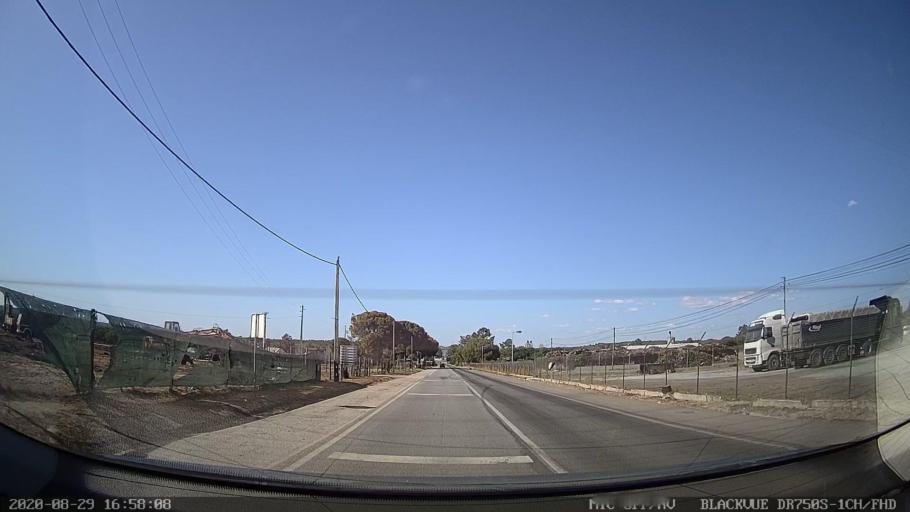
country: PT
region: Setubal
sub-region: Alcacer do Sal
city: Alcacer do Sal
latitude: 38.3979
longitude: -8.5145
